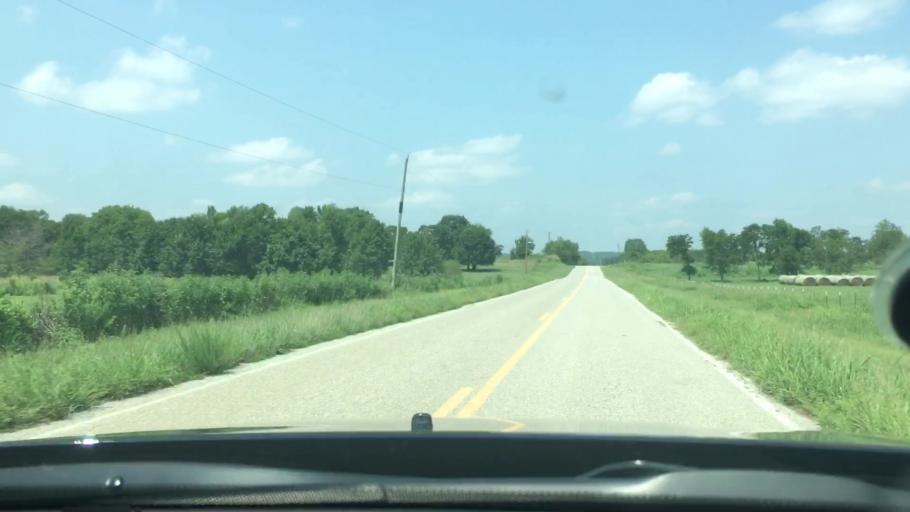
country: US
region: Oklahoma
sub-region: Johnston County
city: Tishomingo
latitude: 34.3947
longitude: -96.4962
